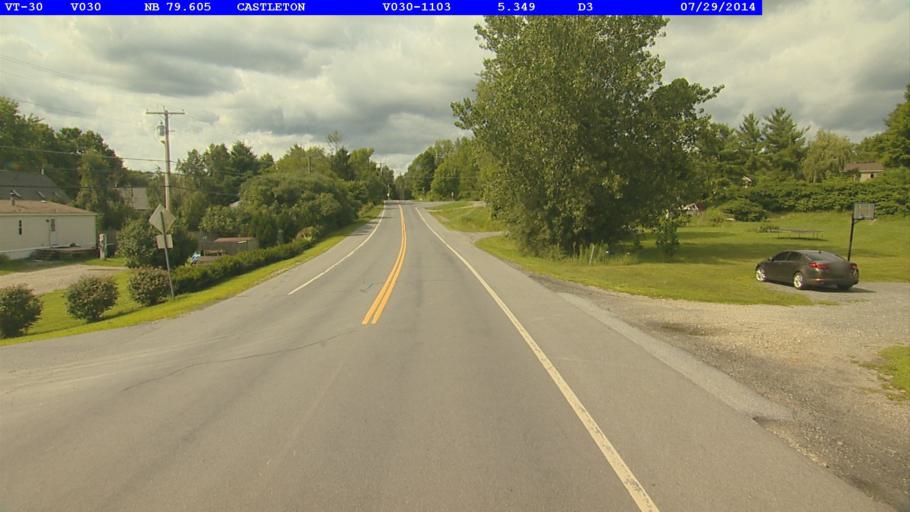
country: US
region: Vermont
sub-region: Rutland County
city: Castleton
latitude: 43.6618
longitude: -73.1902
